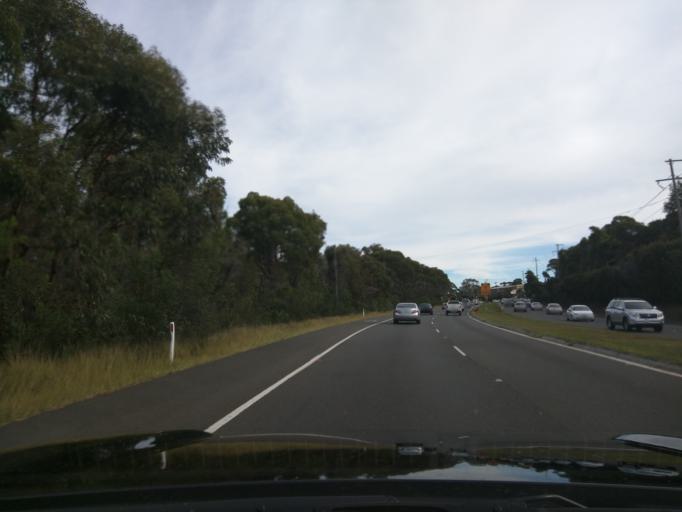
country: AU
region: New South Wales
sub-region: Sutherland Shire
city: Loftus
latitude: -34.0437
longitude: 151.0553
